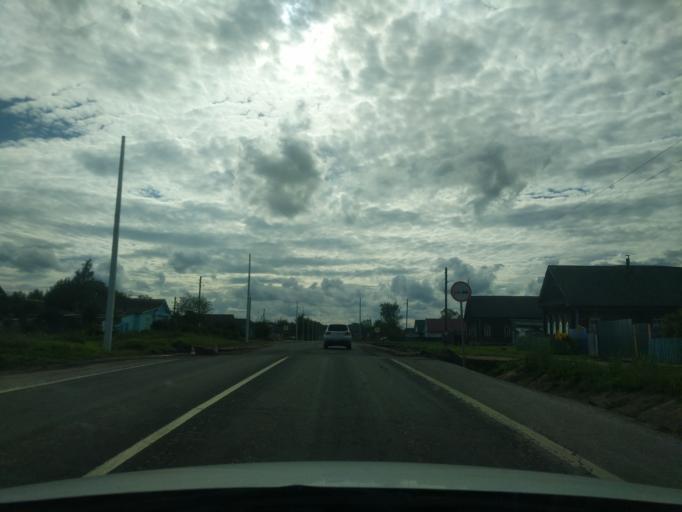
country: RU
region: Jaroslavl
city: Levashevo
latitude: 57.6539
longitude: 40.5585
